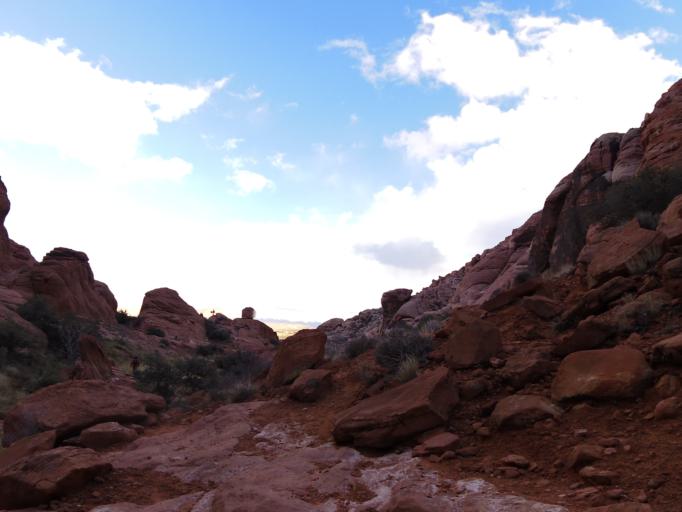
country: US
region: Nevada
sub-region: Clark County
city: Summerlin South
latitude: 36.1519
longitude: -115.4285
